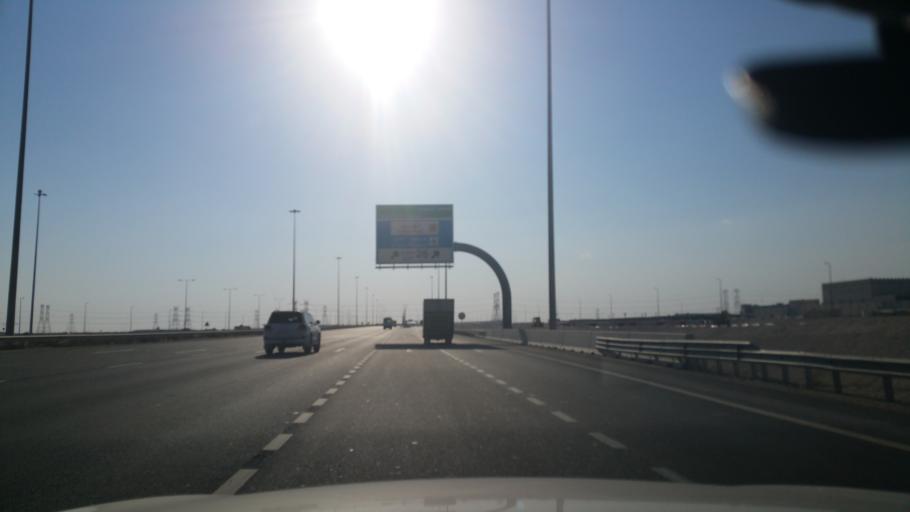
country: QA
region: Baladiyat ar Rayyan
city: Ar Rayyan
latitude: 25.1805
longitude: 51.3470
